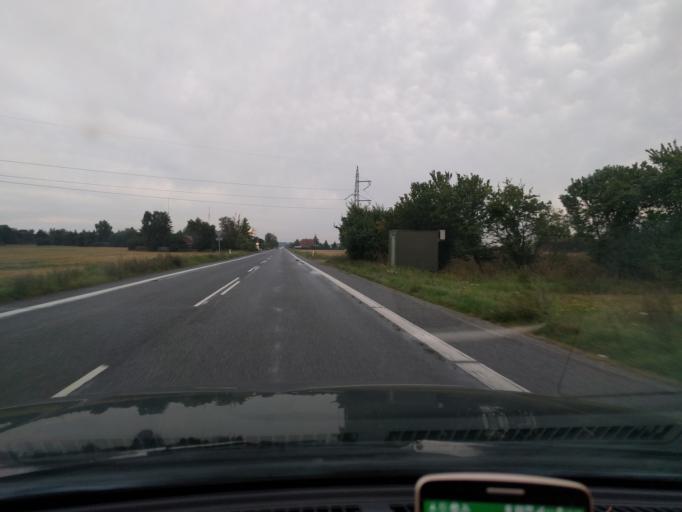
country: DK
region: Zealand
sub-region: Guldborgsund Kommune
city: Norre Alslev
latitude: 54.9448
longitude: 11.8620
